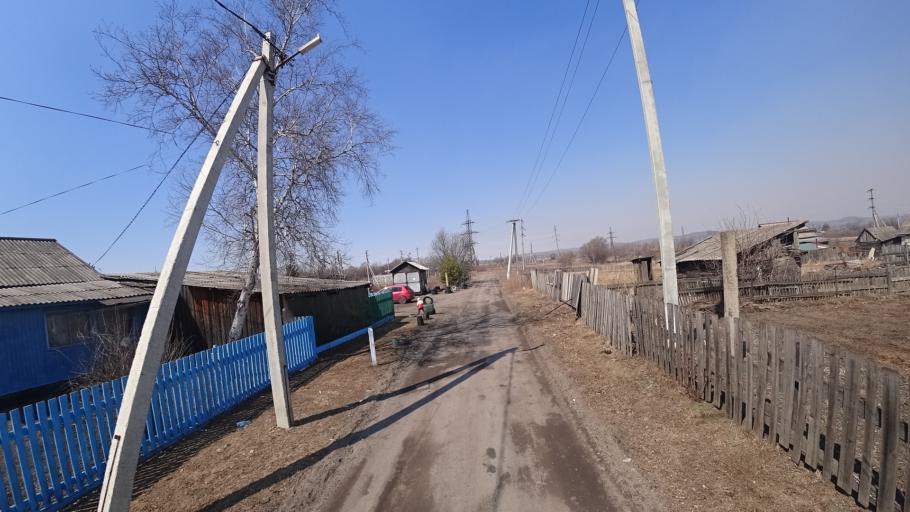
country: RU
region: Amur
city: Novobureyskiy
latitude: 49.7888
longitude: 129.8405
